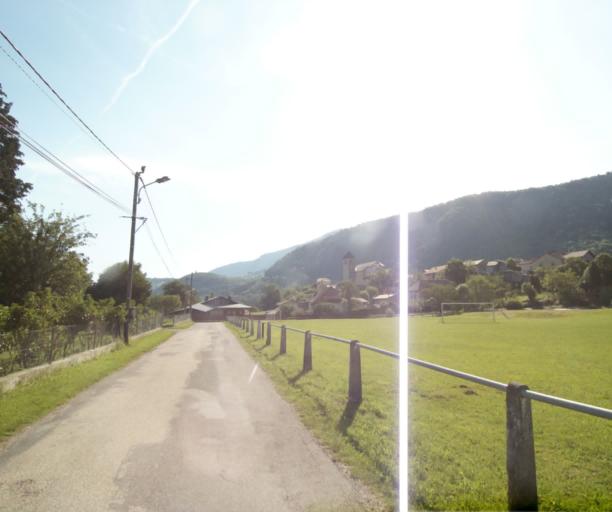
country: FR
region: Rhone-Alpes
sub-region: Departement de la Haute-Savoie
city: Allinges
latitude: 46.3126
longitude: 6.4872
